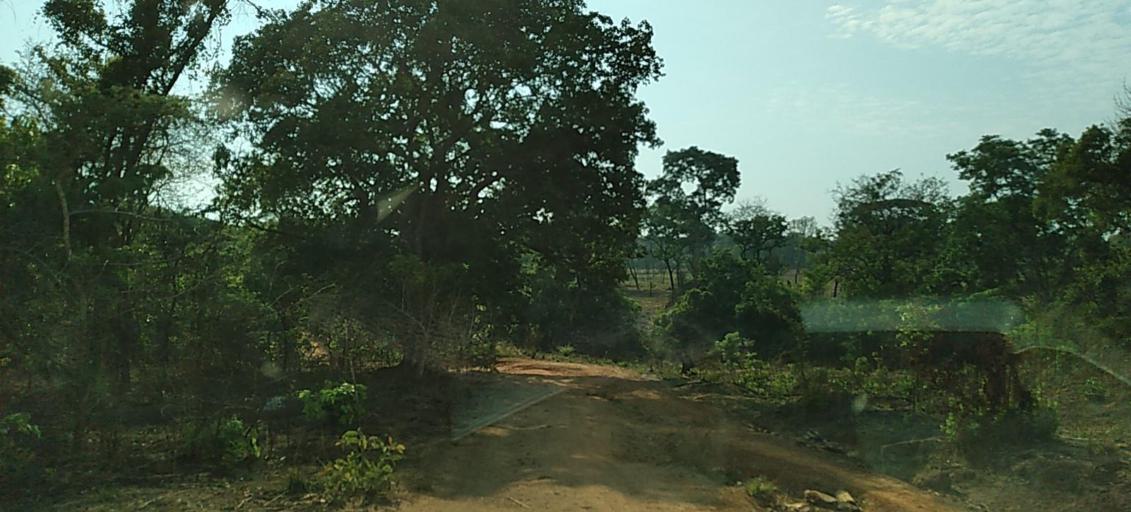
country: ZM
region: Copperbelt
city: Kalulushi
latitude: -13.0071
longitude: 27.7190
